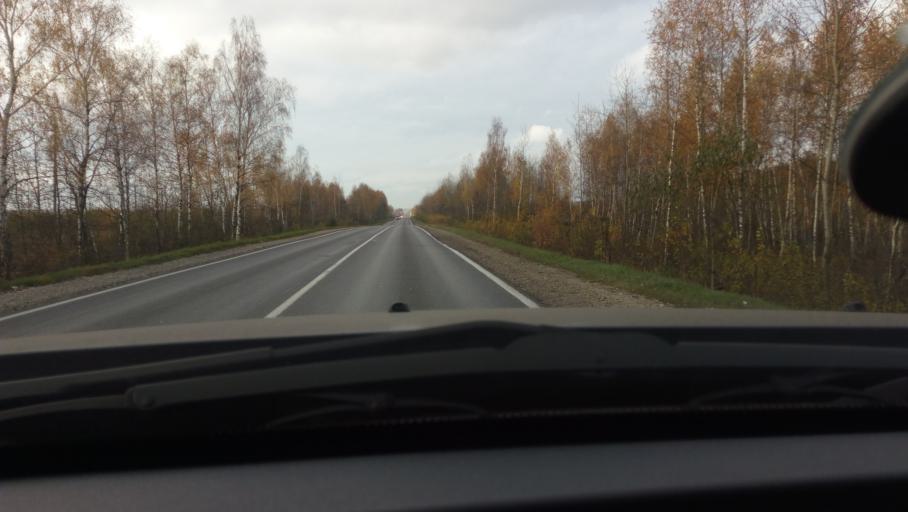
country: RU
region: Moskovskaya
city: Rakhmanovo
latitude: 55.7490
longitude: 38.5993
